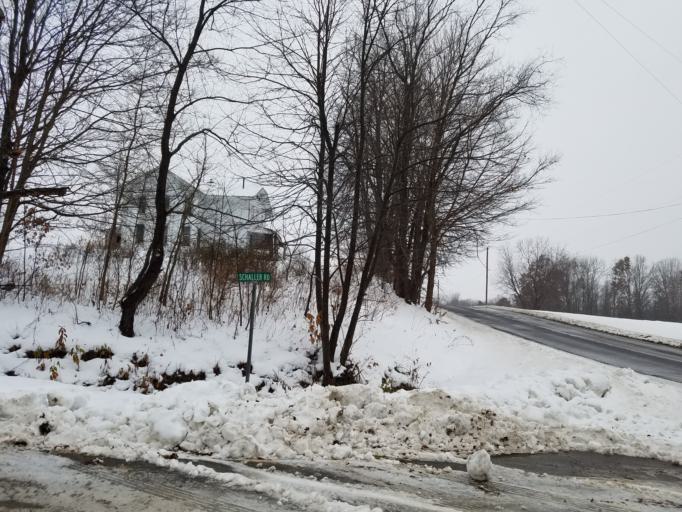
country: US
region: Pennsylvania
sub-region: Mercer County
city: Reynolds Heights
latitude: 41.3217
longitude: -80.3462
